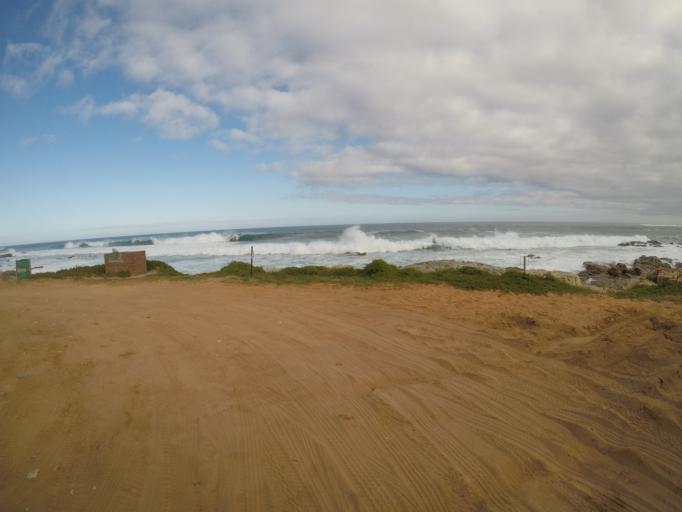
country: ZA
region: Western Cape
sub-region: Eden District Municipality
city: Riversdale
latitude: -34.4321
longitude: 21.3241
